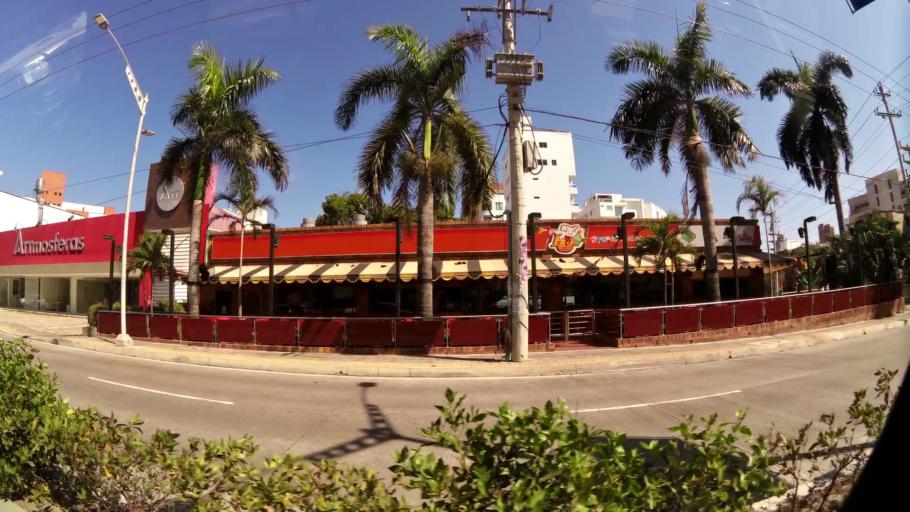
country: CO
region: Atlantico
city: Barranquilla
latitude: 11.0066
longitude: -74.8192
